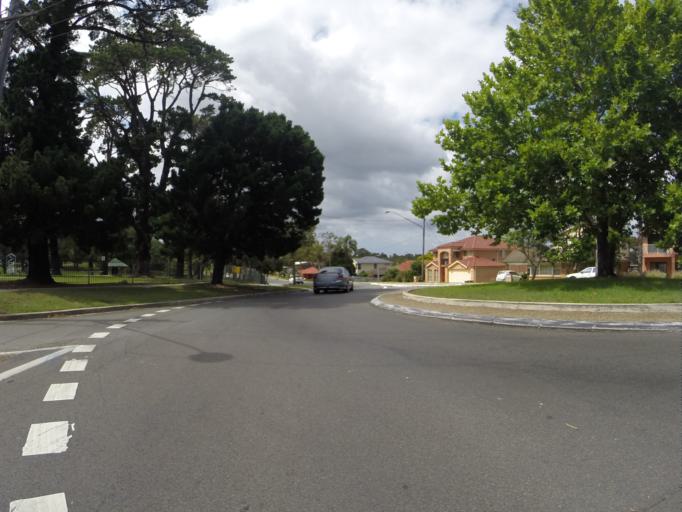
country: AU
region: New South Wales
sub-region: Sutherland Shire
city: Engadine
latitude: -34.0714
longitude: 151.0095
